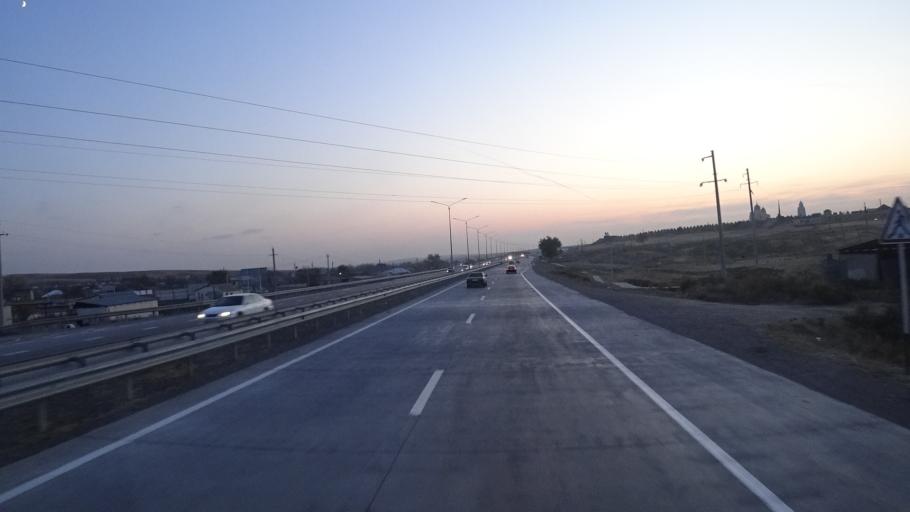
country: KZ
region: Ongtustik Qazaqstan
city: Qazyqurt
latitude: 41.8792
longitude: 69.4349
